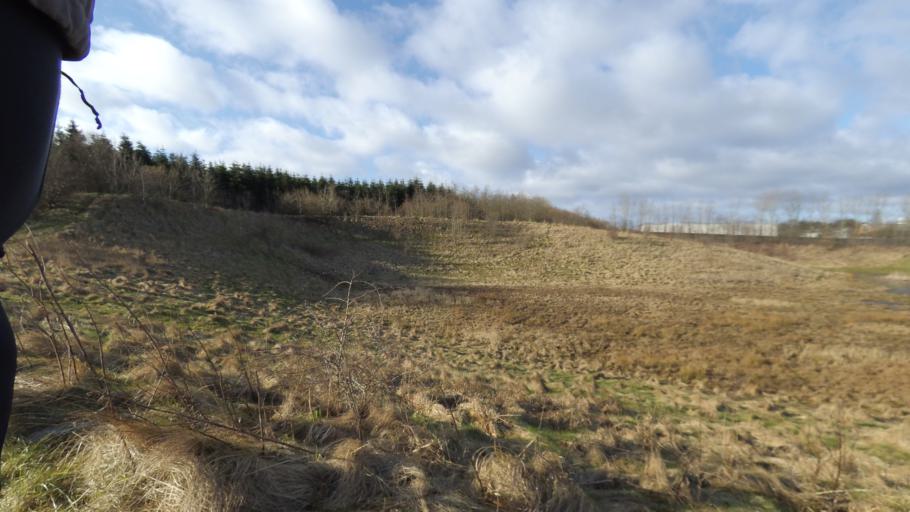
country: DK
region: Central Jutland
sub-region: Arhus Kommune
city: Tranbjerg
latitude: 56.1028
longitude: 10.1251
